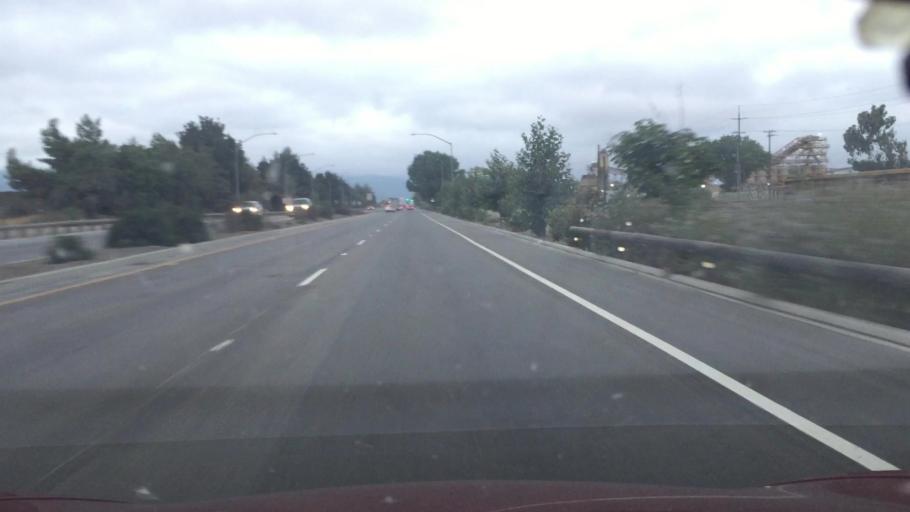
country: US
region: California
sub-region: Alameda County
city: Pleasanton
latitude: 37.6741
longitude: -121.8247
